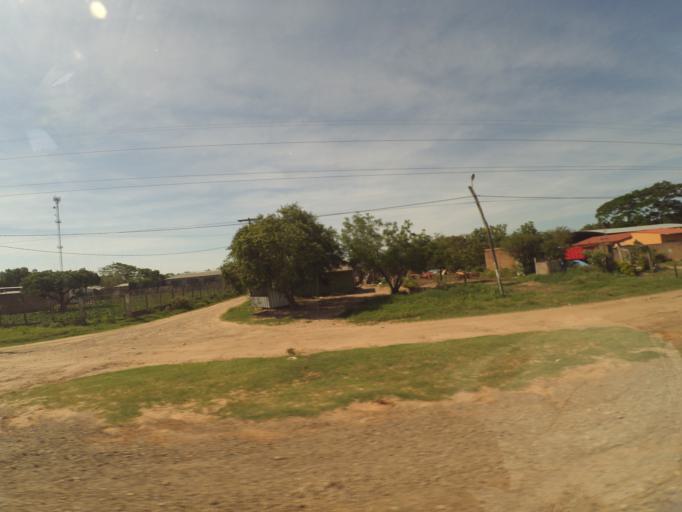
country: BO
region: Santa Cruz
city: San Julian
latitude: -17.7390
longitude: -62.9422
